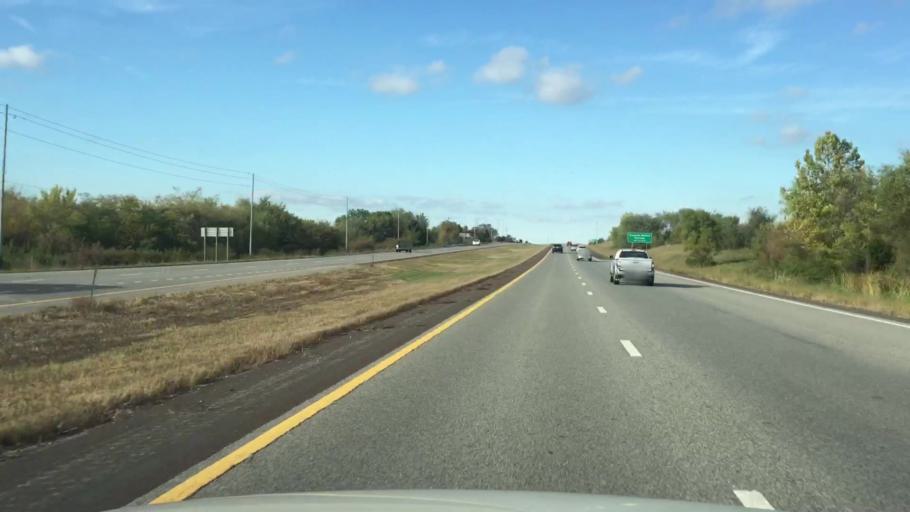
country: US
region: Kansas
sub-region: Wyandotte County
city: Bonner Springs
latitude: 38.9934
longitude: -94.8530
